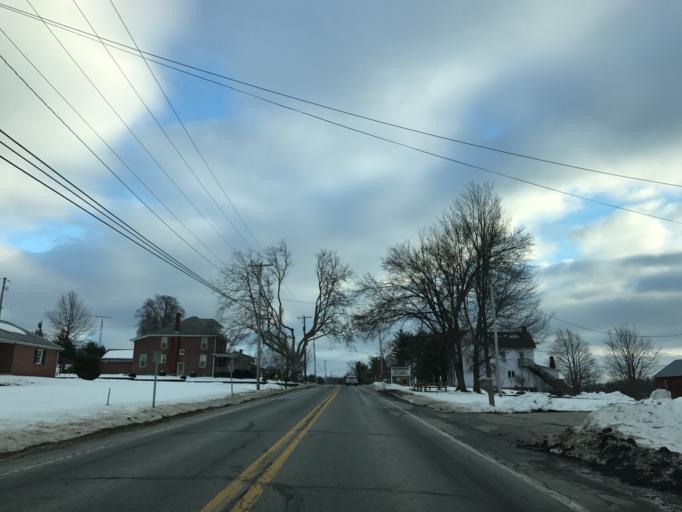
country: US
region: Pennsylvania
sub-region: York County
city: Shrewsbury
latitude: 39.7993
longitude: -76.6794
